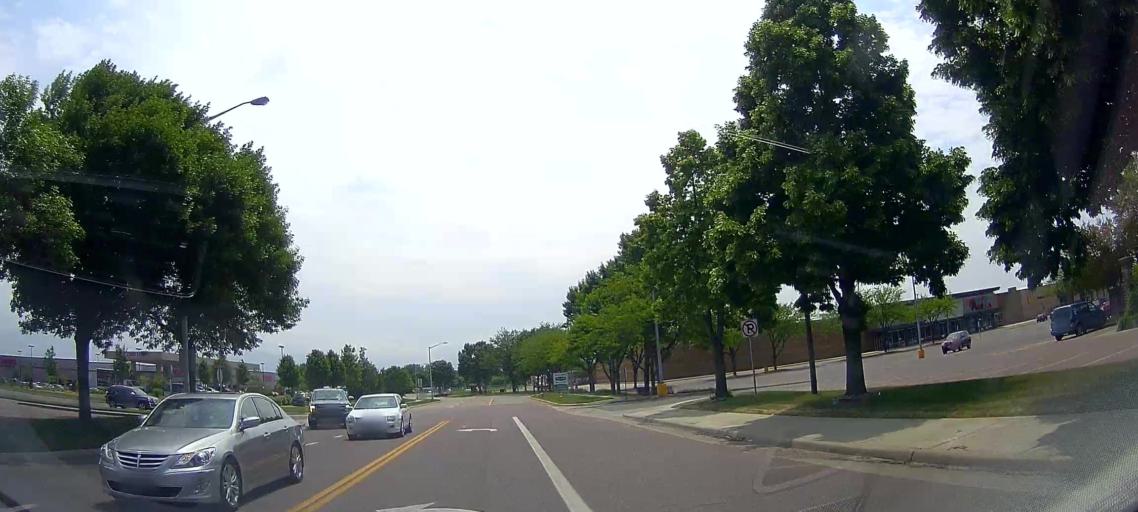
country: US
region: South Dakota
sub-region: Minnehaha County
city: Sioux Falls
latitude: 43.5144
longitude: -96.7411
